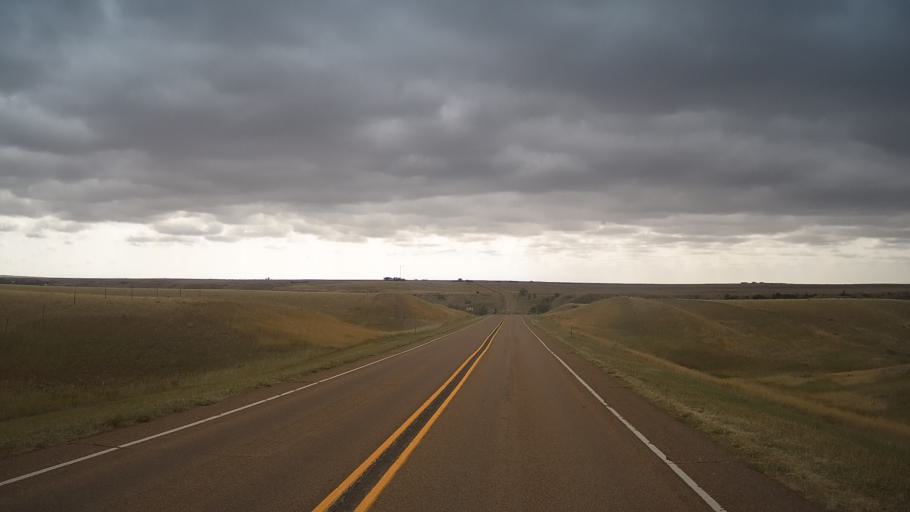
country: US
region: Montana
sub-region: Valley County
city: Glasgow
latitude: 48.3665
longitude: -106.7874
